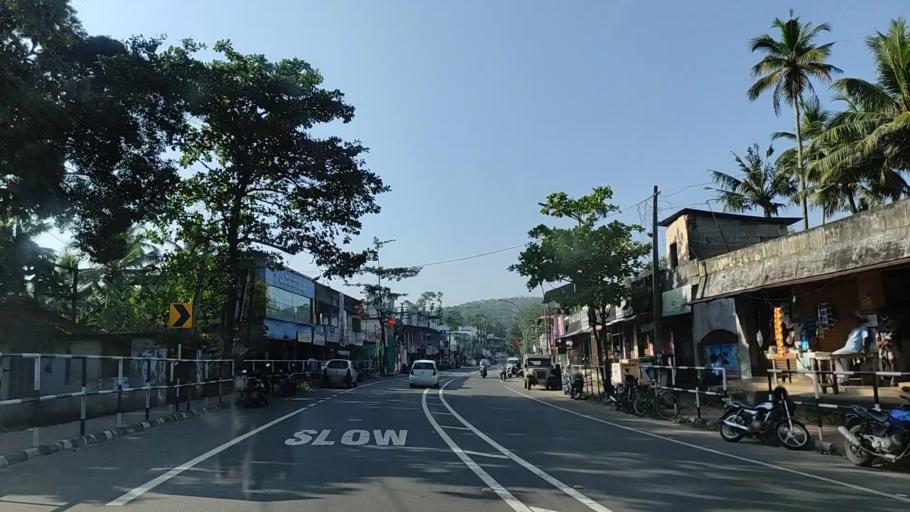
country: IN
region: Kerala
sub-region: Kollam
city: Punalur
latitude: 8.9257
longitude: 76.8549
